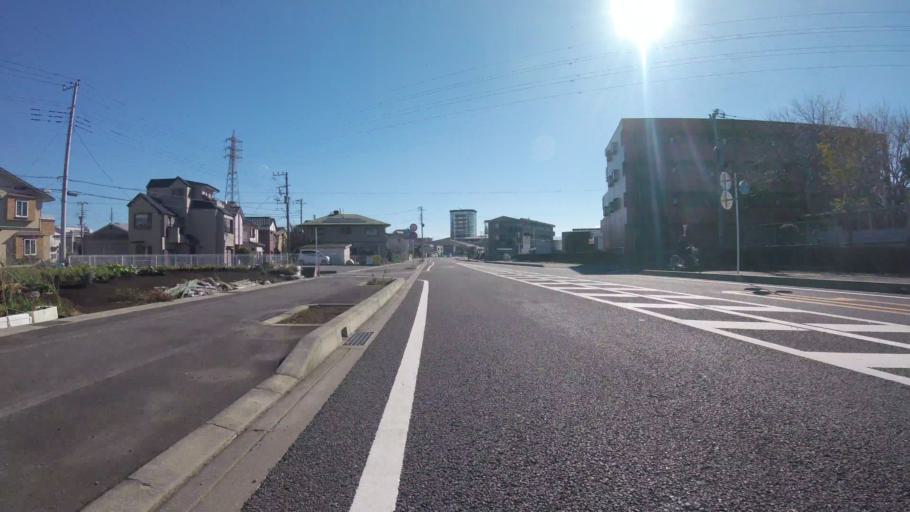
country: JP
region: Shizuoka
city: Mishima
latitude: 35.1383
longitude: 138.9092
